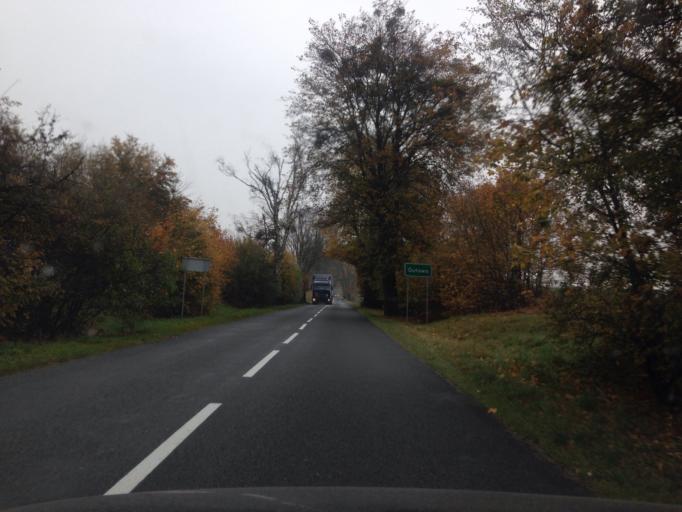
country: PL
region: Kujawsko-Pomorskie
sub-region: Powiat brodnicki
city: Bartniczka
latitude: 53.2453
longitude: 19.6487
